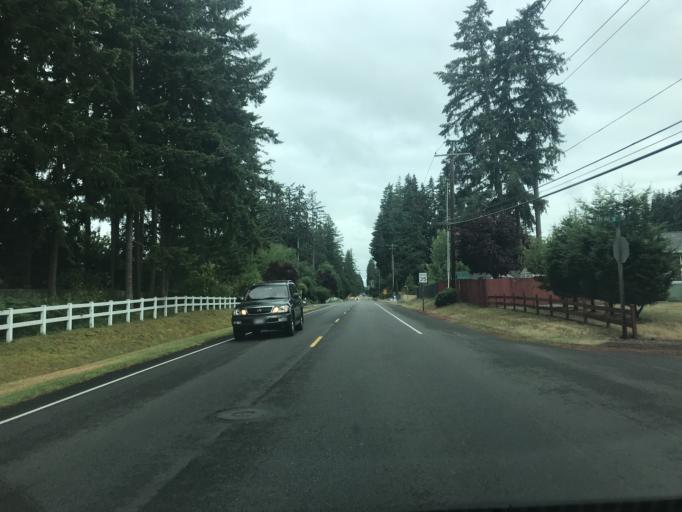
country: US
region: Washington
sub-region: King County
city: Black Diamond
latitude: 47.3435
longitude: -122.0282
